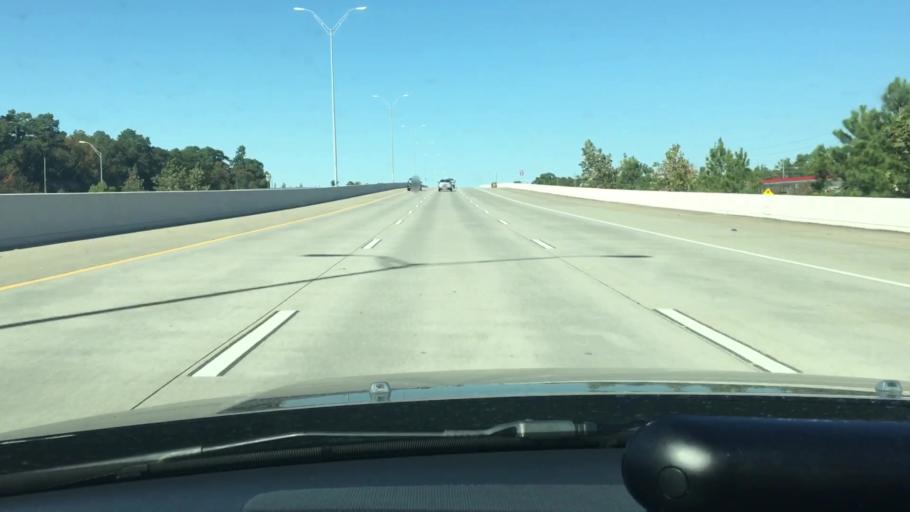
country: US
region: Texas
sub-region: Harris County
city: Sheldon
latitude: 29.8806
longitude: -95.1956
